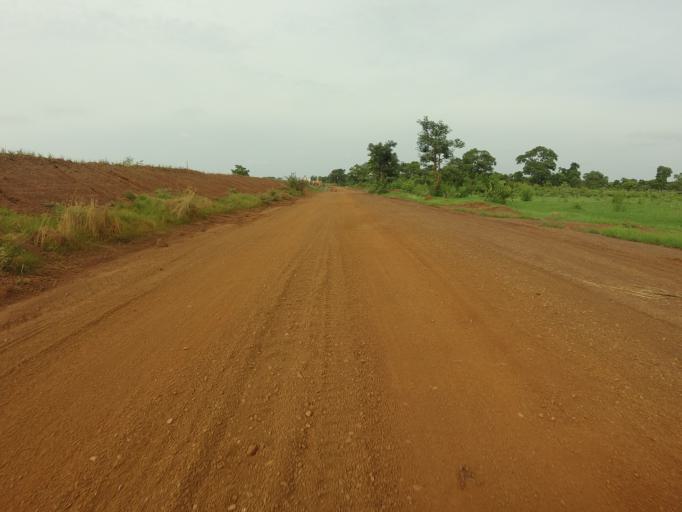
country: GH
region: Northern
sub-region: Yendi
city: Yendi
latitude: 9.7949
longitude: -0.1140
